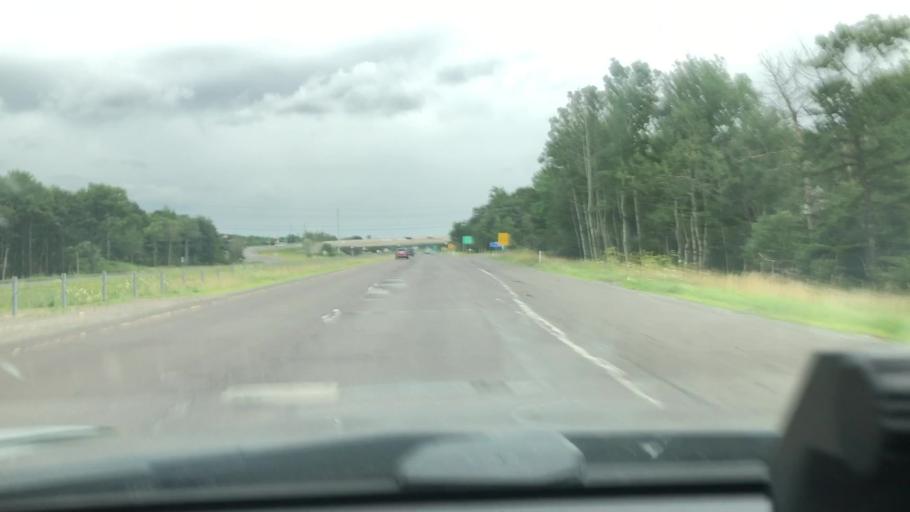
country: US
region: Pennsylvania
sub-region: Monroe County
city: Emerald Lakes
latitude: 41.1099
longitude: -75.3984
